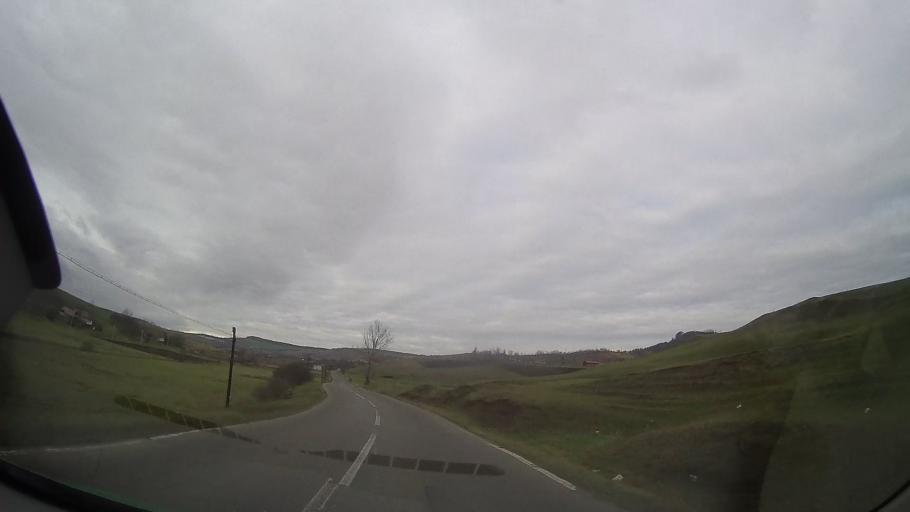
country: RO
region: Bistrita-Nasaud
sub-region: Comuna Urmenis
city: Urmenis
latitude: 46.7628
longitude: 24.3788
